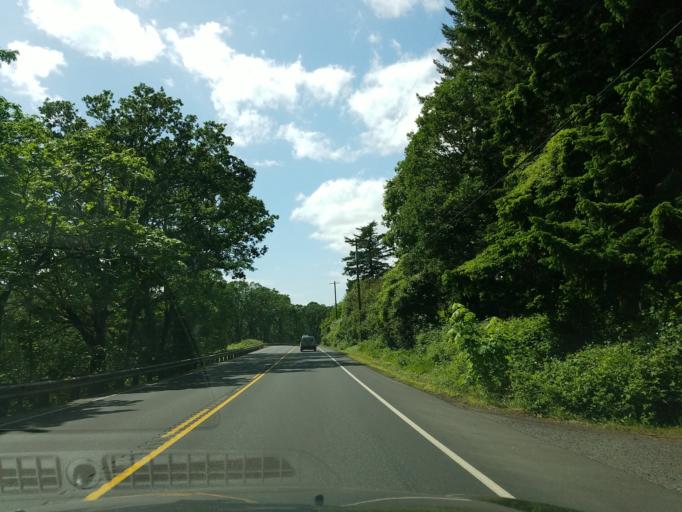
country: US
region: Washington
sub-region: Clark County
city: Washougal
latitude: 45.5598
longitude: -122.2570
